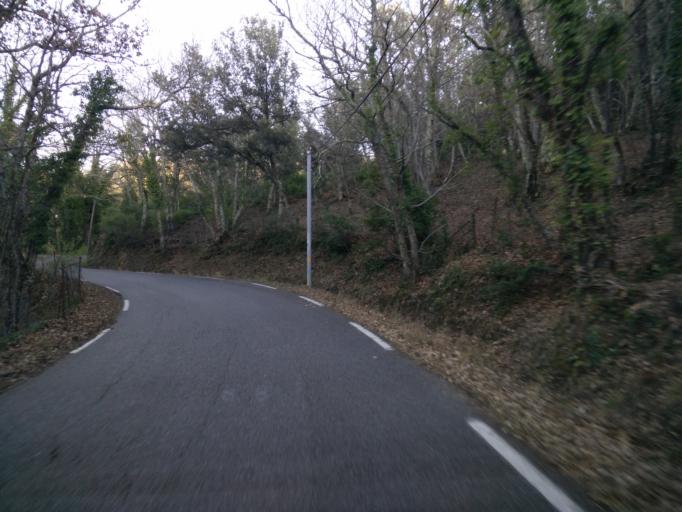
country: FR
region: Provence-Alpes-Cote d'Azur
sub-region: Departement du Var
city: Collobrieres
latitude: 43.2258
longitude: 6.2947
